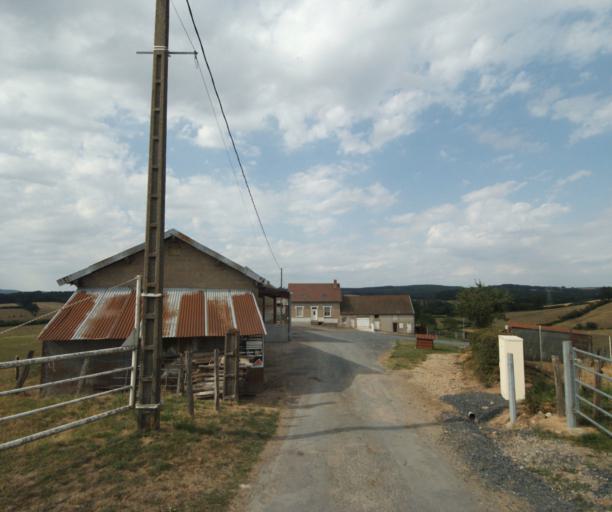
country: FR
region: Bourgogne
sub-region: Departement de Saone-et-Loire
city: Gueugnon
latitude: 46.6034
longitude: 4.1012
